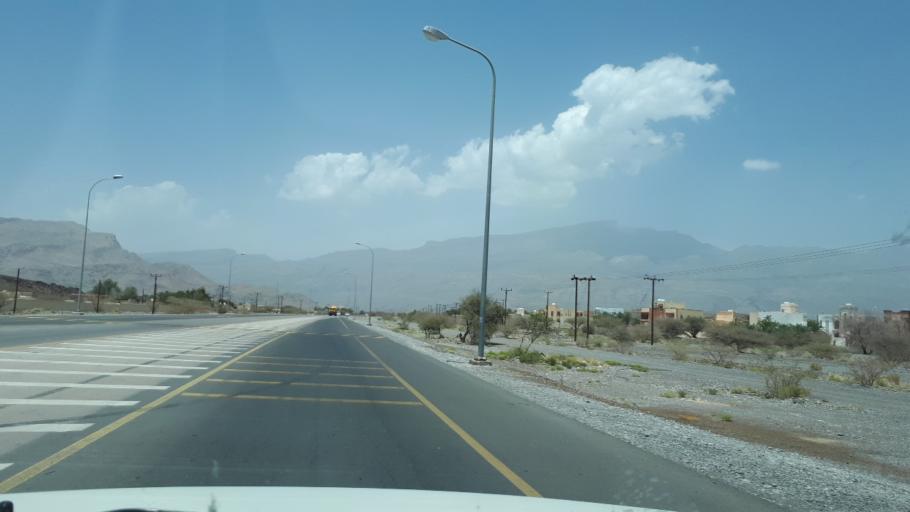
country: OM
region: Muhafazat ad Dakhiliyah
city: Bahla'
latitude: 23.0719
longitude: 57.2732
